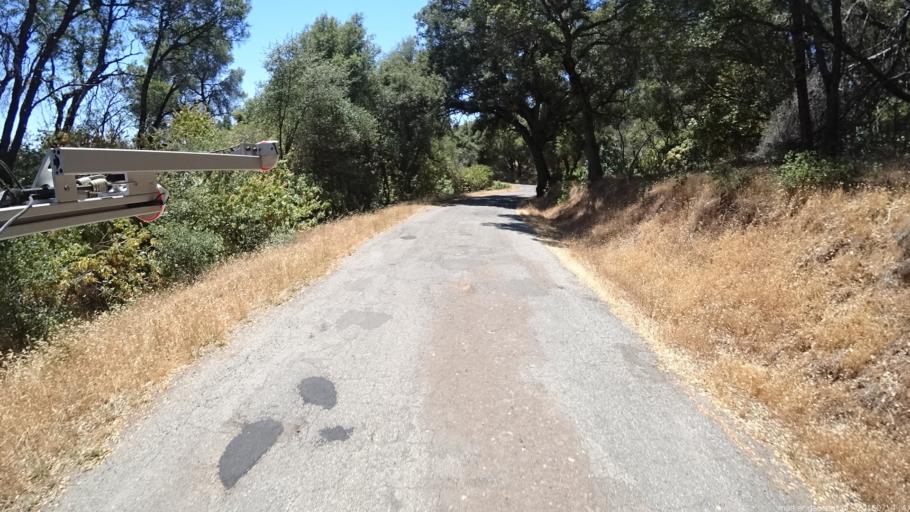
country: US
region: California
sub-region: Madera County
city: Ahwahnee
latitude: 37.4147
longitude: -119.7211
